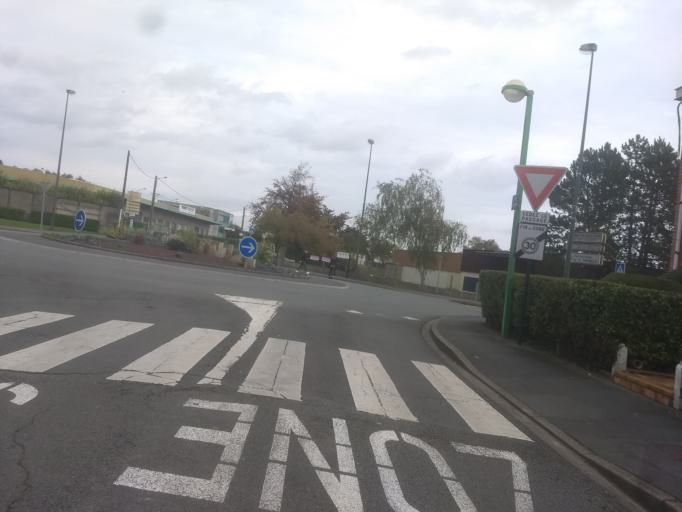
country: FR
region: Nord-Pas-de-Calais
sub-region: Departement du Pas-de-Calais
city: Achicourt
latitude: 50.2730
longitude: 2.7655
